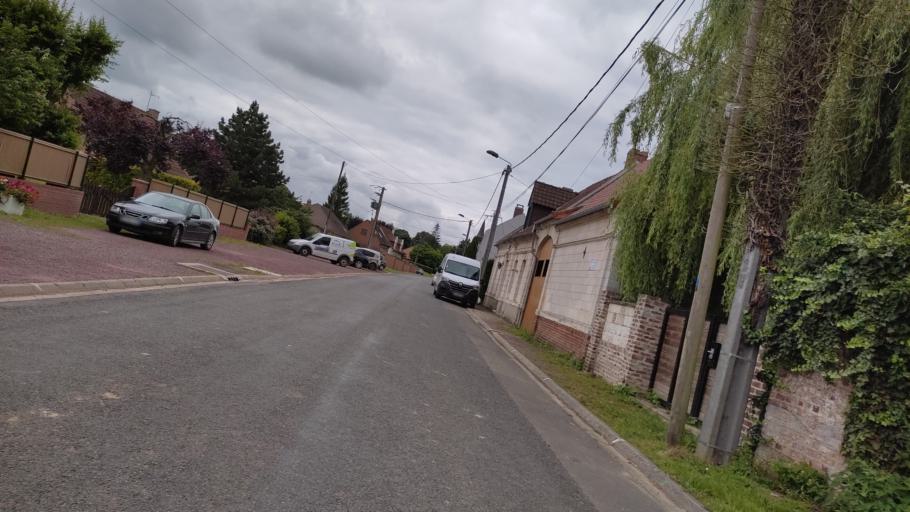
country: FR
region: Nord-Pas-de-Calais
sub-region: Departement du Pas-de-Calais
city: Beaumetz-les-Loges
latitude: 50.2569
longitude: 2.6480
